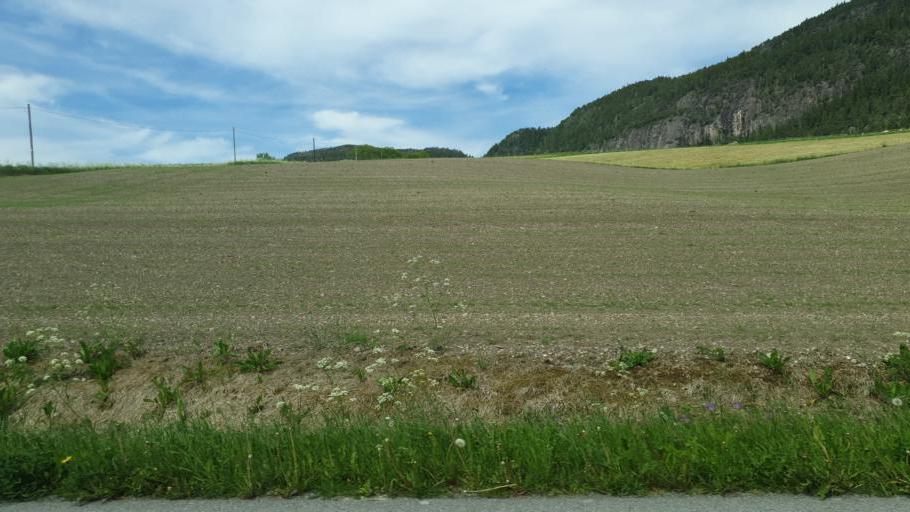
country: NO
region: Sor-Trondelag
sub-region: Trondheim
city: Trondheim
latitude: 63.5883
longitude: 10.4238
